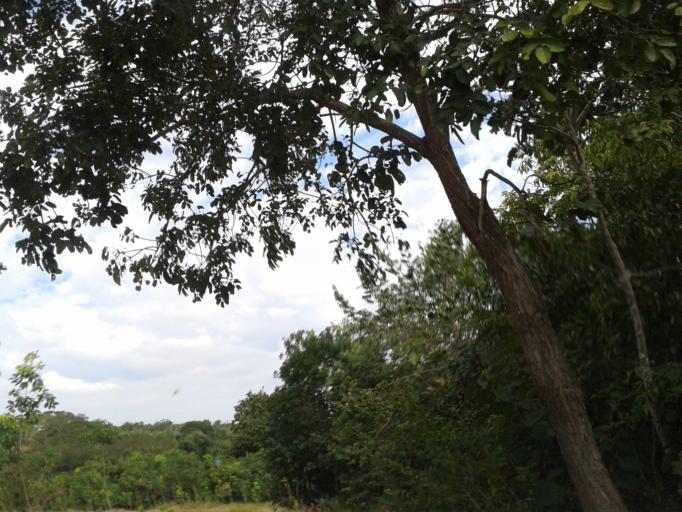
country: BR
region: Minas Gerais
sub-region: Campina Verde
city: Campina Verde
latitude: -19.3841
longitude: -49.6618
